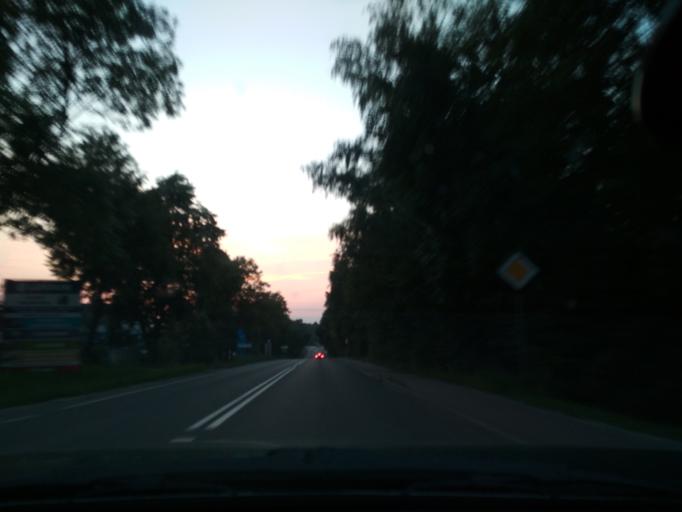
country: PL
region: Silesian Voivodeship
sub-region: Powiat zawiercianski
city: Ogrodzieniec
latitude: 50.4751
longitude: 19.4764
